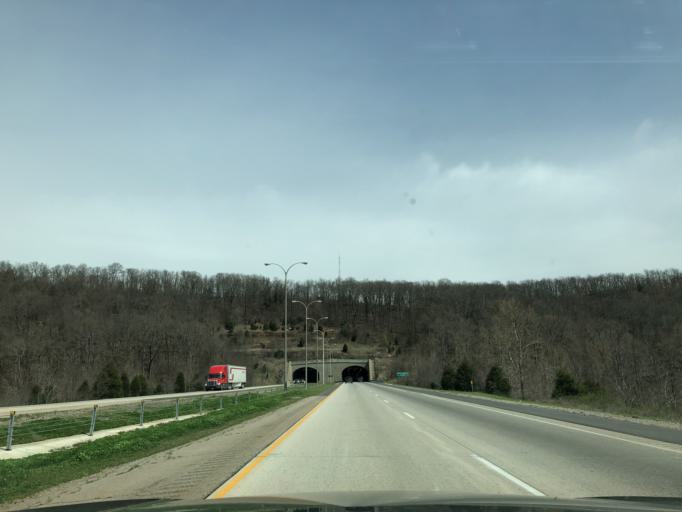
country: US
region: Arkansas
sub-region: Washington County
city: West Fork
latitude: 35.7634
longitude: -94.1921
